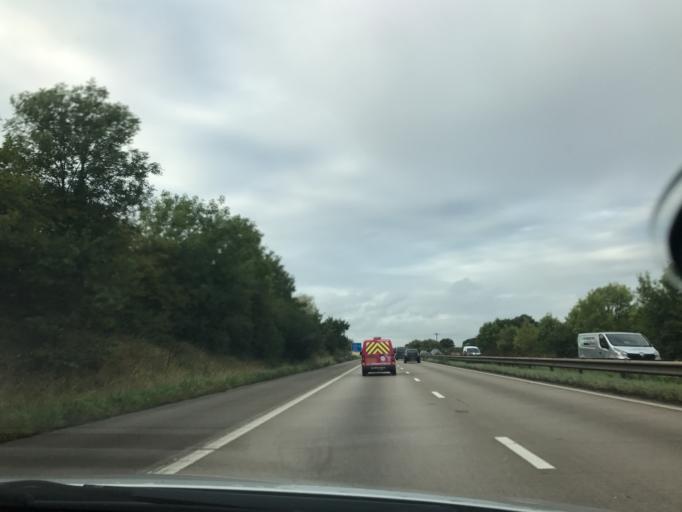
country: GB
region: England
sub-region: Cheshire West and Chester
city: Stoke
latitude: 53.2245
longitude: -2.8608
